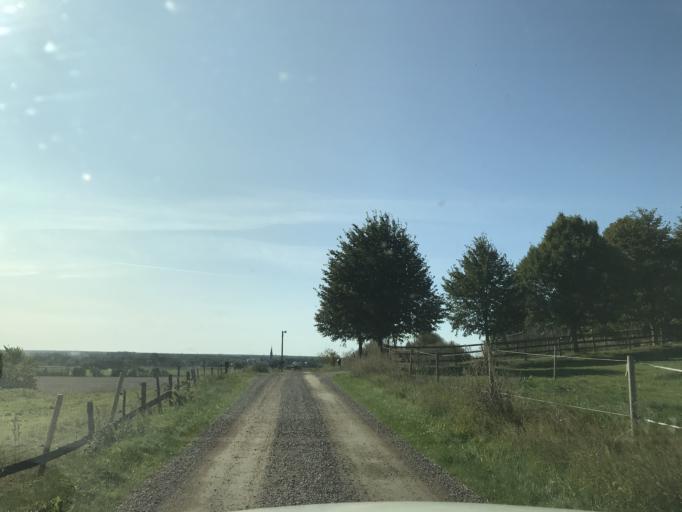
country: SE
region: Skane
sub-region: Landskrona
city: Asmundtorp
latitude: 55.9028
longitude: 12.9493
